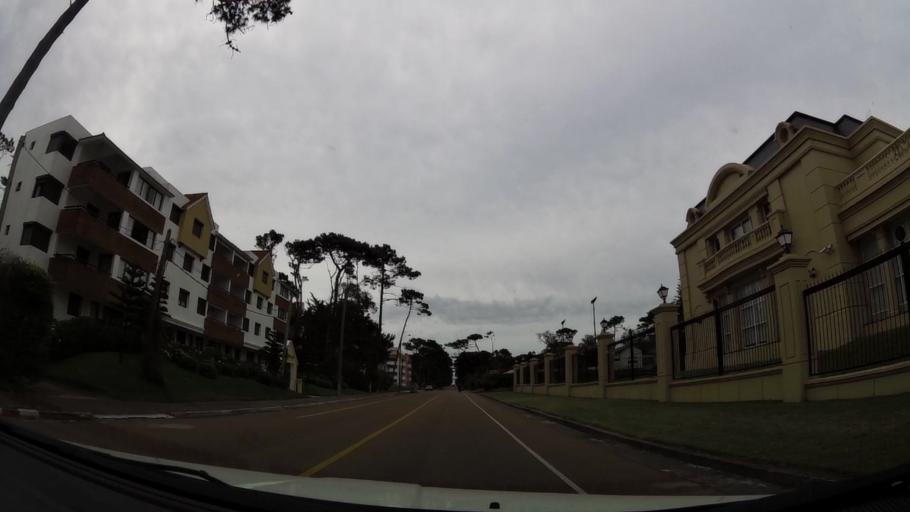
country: UY
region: Maldonado
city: Maldonado
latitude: -34.9306
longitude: -54.9560
